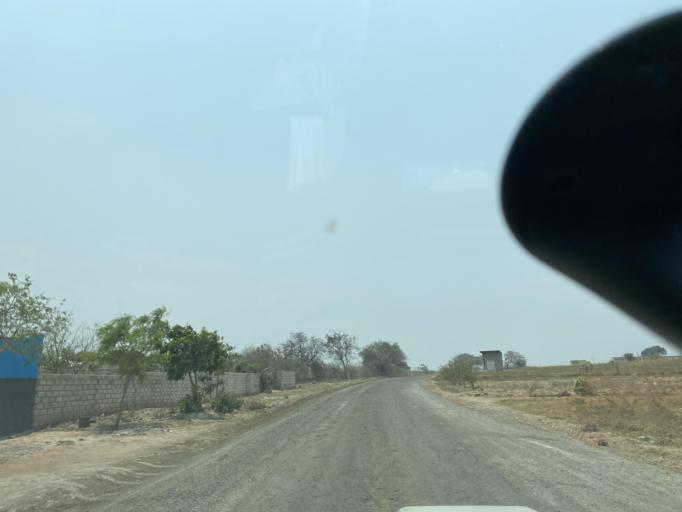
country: ZM
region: Lusaka
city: Lusaka
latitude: -15.5478
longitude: 28.4445
